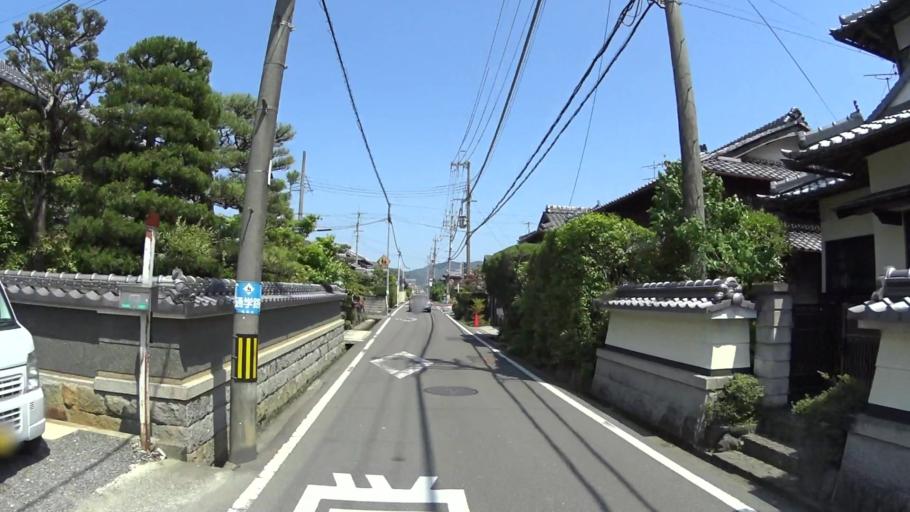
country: JP
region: Kyoto
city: Kameoka
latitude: 35.0183
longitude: 135.5554
